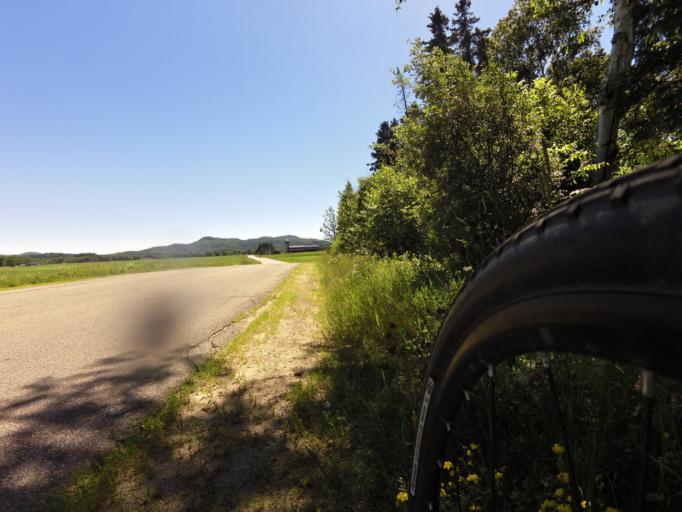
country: CA
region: Quebec
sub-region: Laurentides
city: Mont-Tremblant
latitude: 46.0794
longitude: -74.6325
